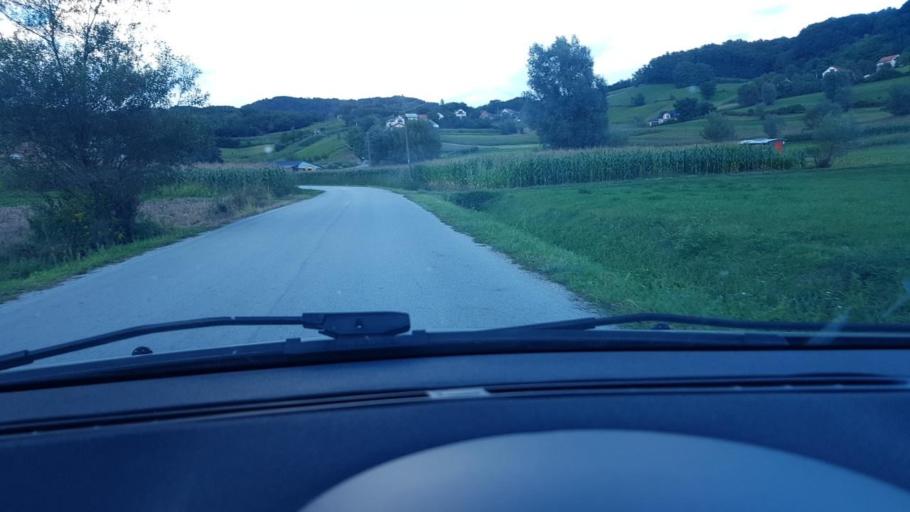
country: HR
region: Krapinsko-Zagorska
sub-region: Grad Krapina
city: Krapina
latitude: 46.1542
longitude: 15.8257
